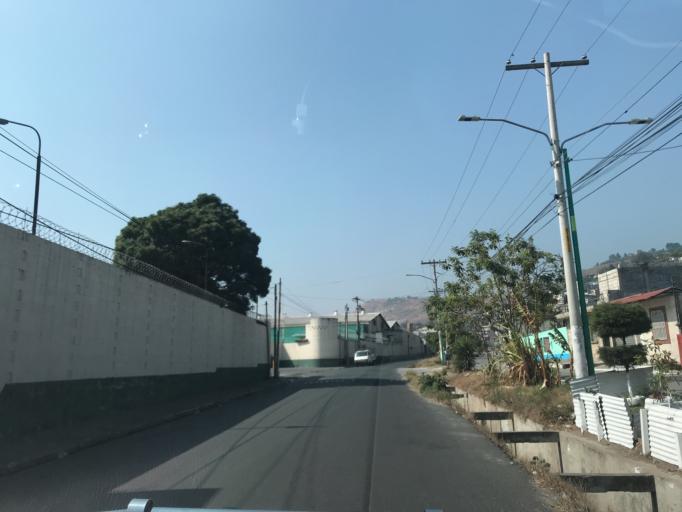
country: GT
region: Guatemala
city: Villa Nueva
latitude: 14.5001
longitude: -90.5850
